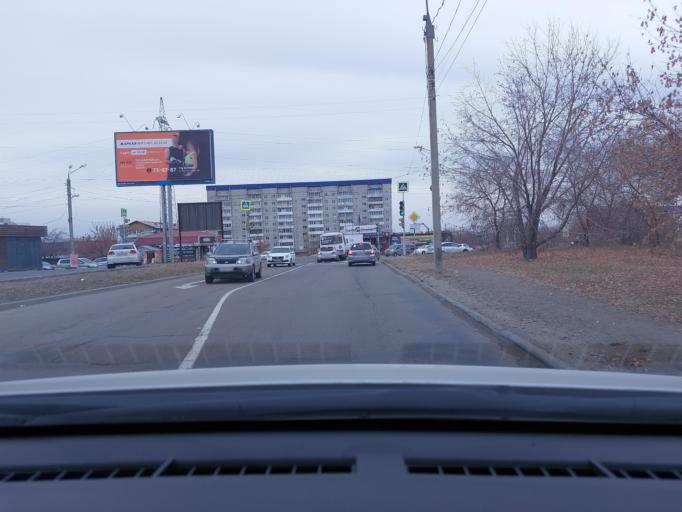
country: RU
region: Irkutsk
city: Smolenshchina
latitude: 52.3476
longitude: 104.1658
